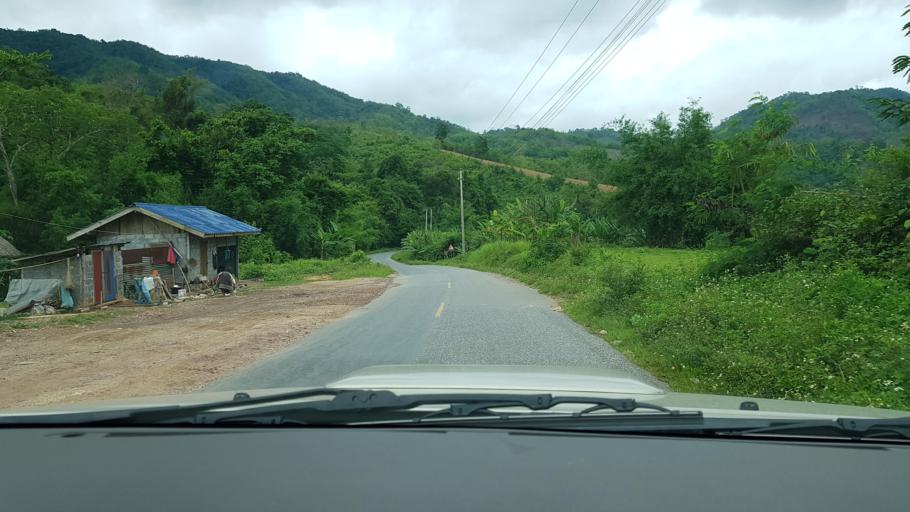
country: LA
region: Loungnamtha
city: Muang Nale
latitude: 20.3815
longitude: 101.7407
